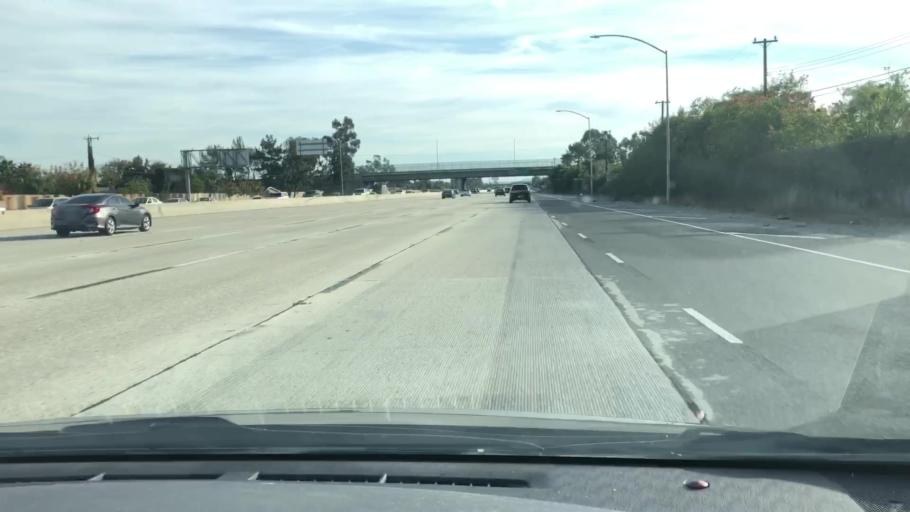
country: US
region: California
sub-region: Orange County
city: Placentia
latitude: 33.8354
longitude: -117.8764
